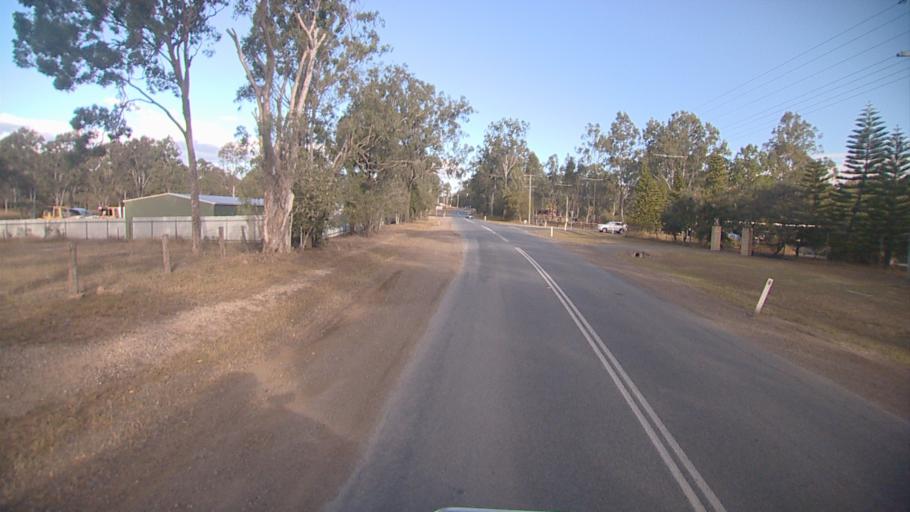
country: AU
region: Queensland
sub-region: Logan
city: Cedar Vale
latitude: -27.8532
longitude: 153.0523
